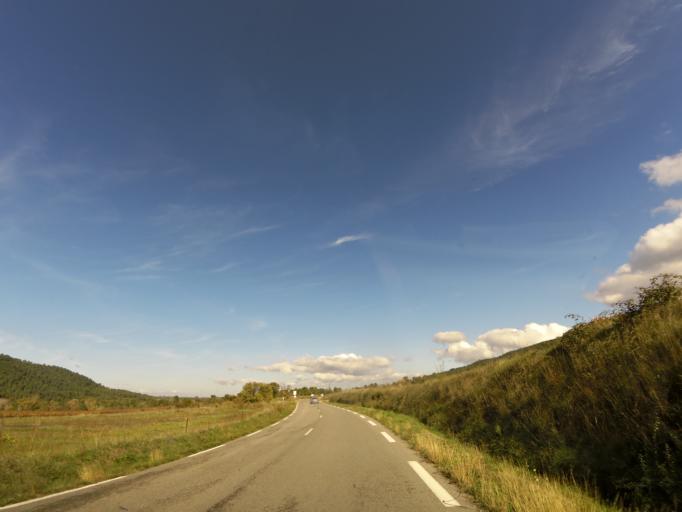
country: FR
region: Languedoc-Roussillon
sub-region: Departement du Gard
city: Ledignan
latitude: 43.9047
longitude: 4.1053
